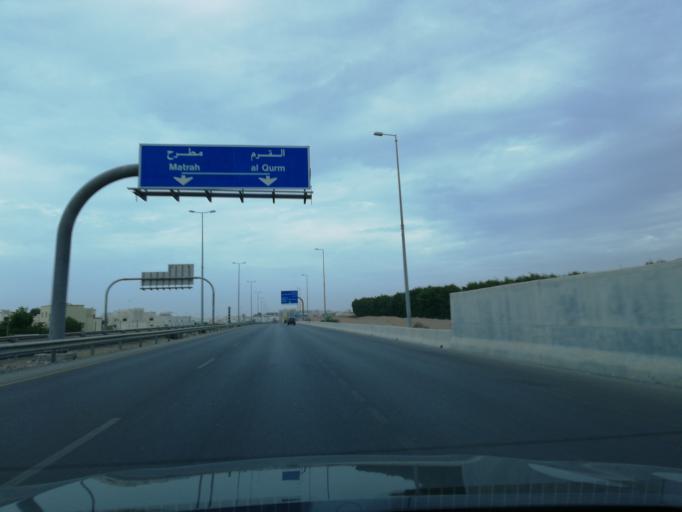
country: OM
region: Muhafazat Masqat
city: Bawshar
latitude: 23.5885
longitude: 58.4363
